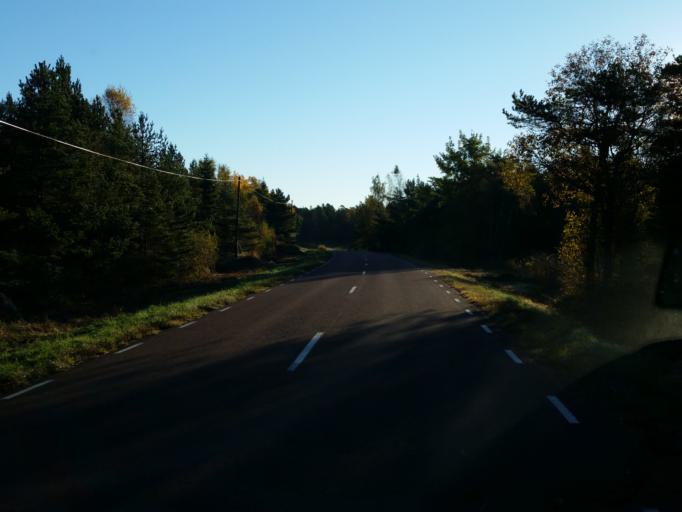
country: AX
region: Alands skaergard
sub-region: Vardoe
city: Vardoe
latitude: 60.2277
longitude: 20.4014
